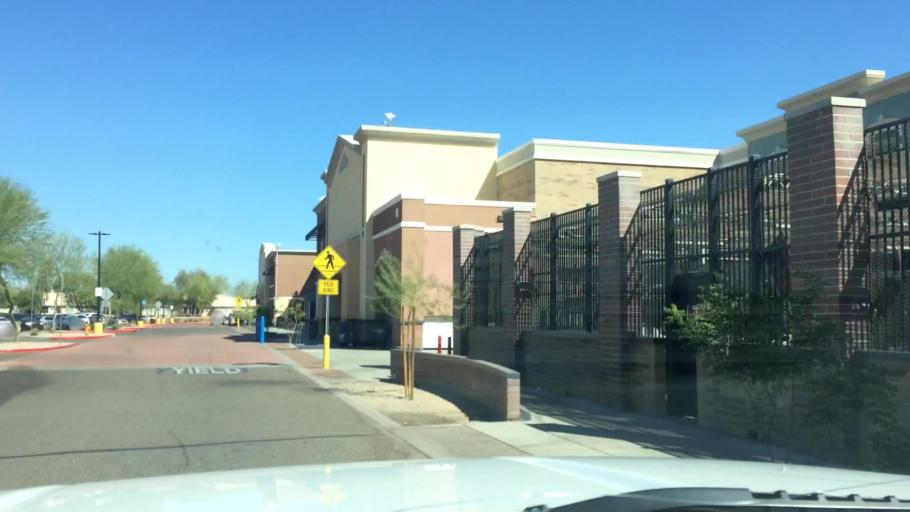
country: US
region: Arizona
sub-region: Maricopa County
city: Peoria
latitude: 33.5791
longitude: -112.2311
